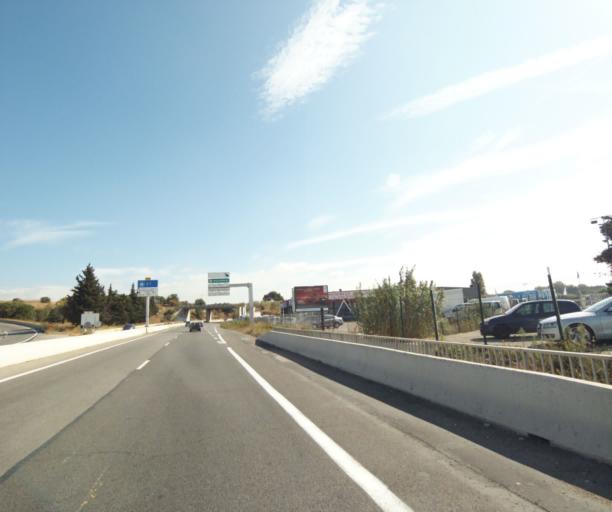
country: FR
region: Provence-Alpes-Cote d'Azur
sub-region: Departement des Bouches-du-Rhone
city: Saint-Victoret
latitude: 43.4238
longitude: 5.2332
